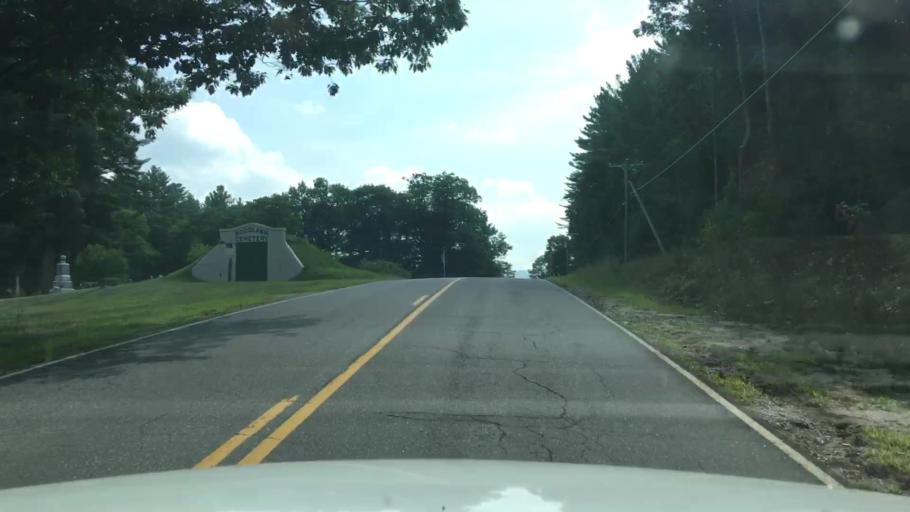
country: US
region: Maine
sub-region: Oxford County
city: Rumford
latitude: 44.6230
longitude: -70.7454
